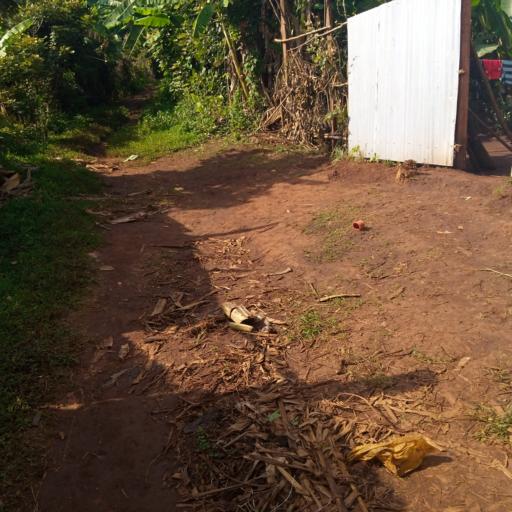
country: ET
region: Oromiya
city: Jima
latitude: 7.6766
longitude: 36.8688
